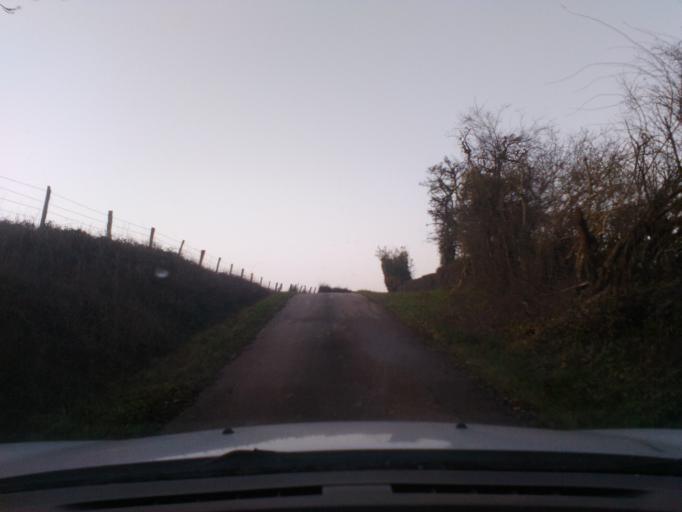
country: FR
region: Lorraine
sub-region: Departement des Vosges
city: Vittel
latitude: 48.2575
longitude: 6.0004
